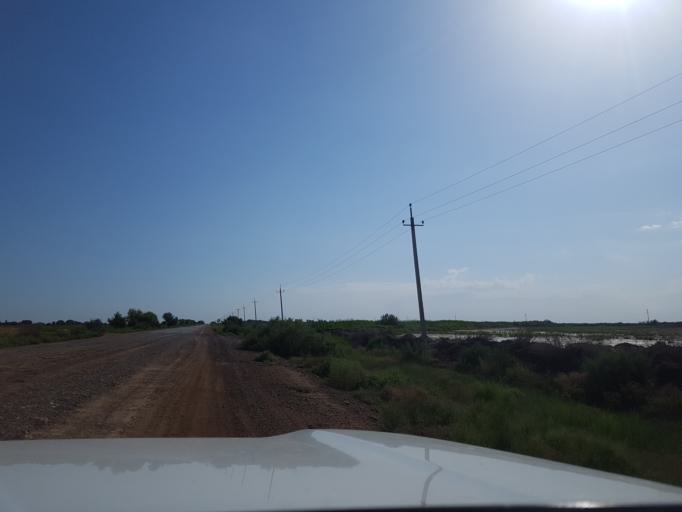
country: TM
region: Dasoguz
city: Koeneuergench
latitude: 42.0355
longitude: 58.8090
